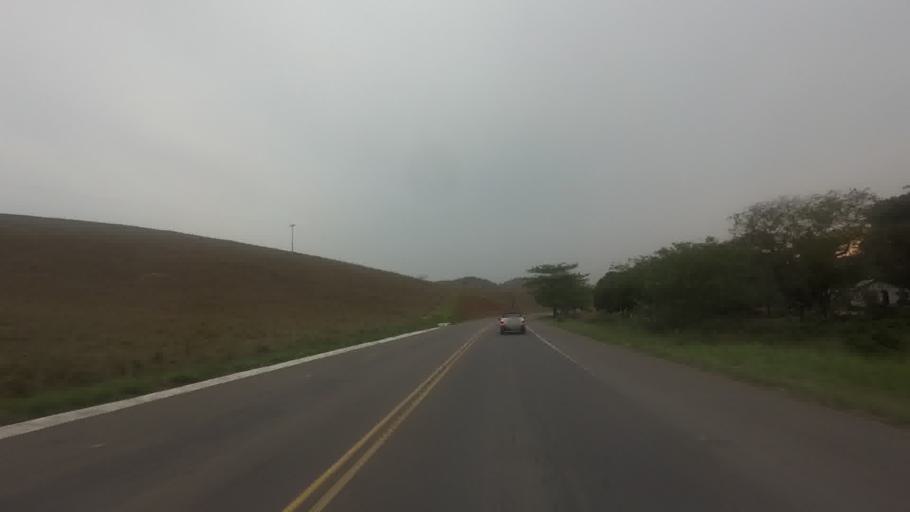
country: BR
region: Minas Gerais
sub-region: Recreio
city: Recreio
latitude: -21.6571
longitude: -42.3704
